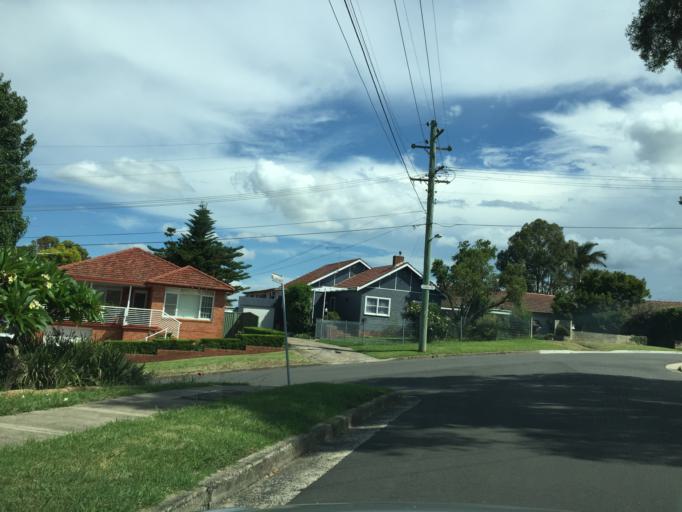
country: AU
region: New South Wales
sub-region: Blacktown
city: Blacktown
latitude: -33.7782
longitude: 150.8928
